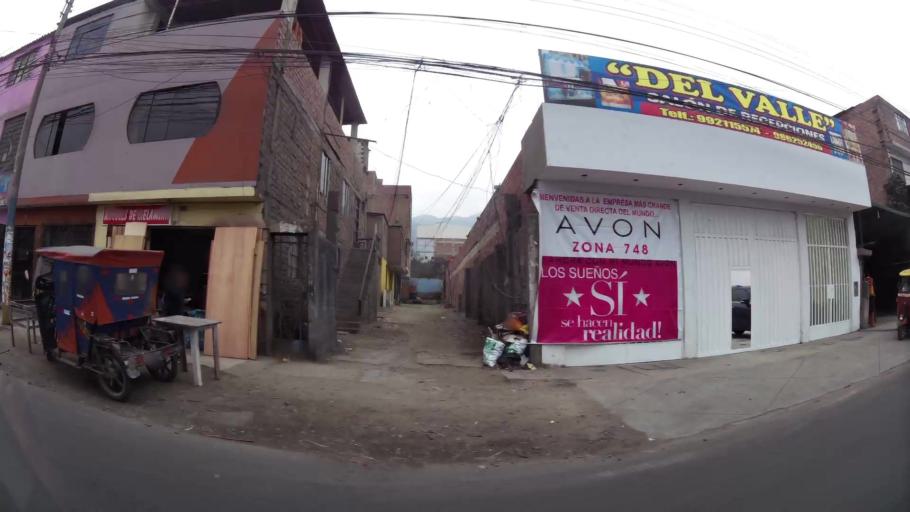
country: PE
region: Lima
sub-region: Lima
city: Independencia
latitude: -11.9801
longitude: -77.0121
